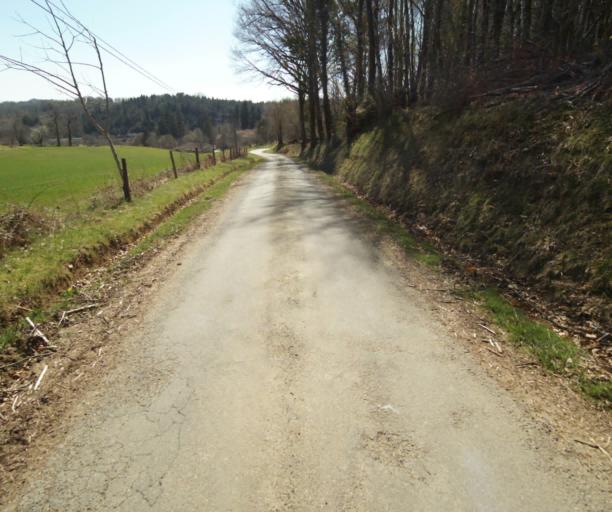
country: FR
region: Limousin
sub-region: Departement de la Correze
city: Saint-Clement
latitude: 45.3171
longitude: 1.7099
